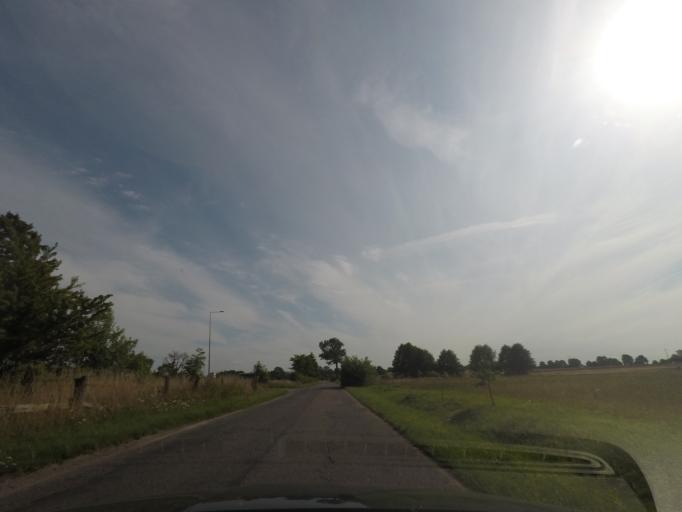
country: PL
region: Pomeranian Voivodeship
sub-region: Powiat slupski
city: Smoldzino
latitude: 54.6252
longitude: 17.2421
